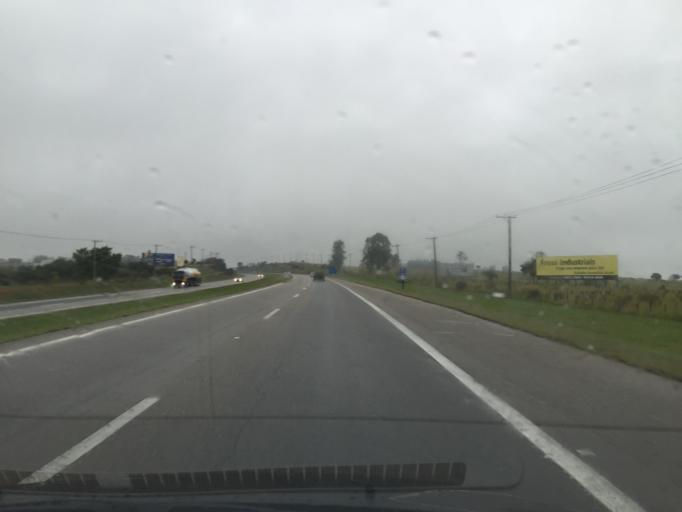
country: BR
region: Sao Paulo
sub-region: Itu
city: Itu
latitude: -23.3016
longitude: -47.3323
